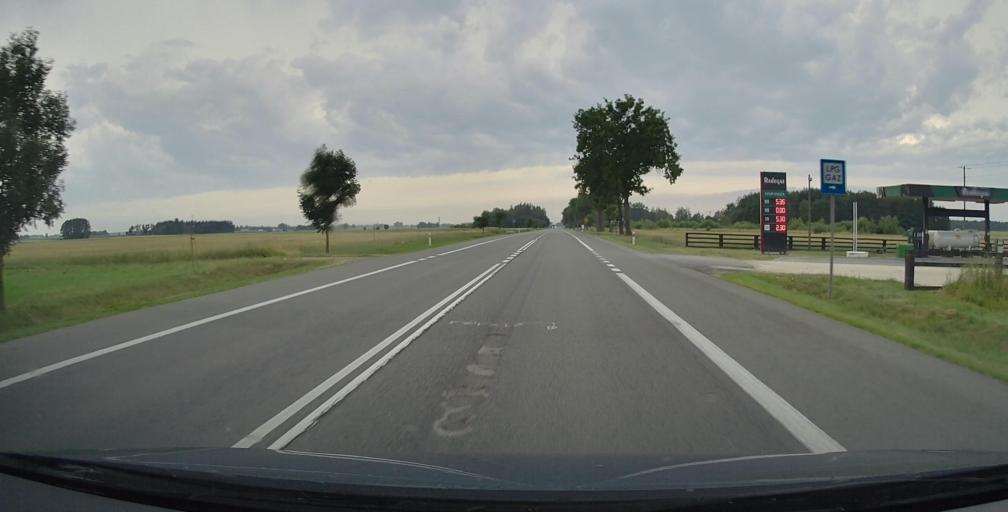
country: PL
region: Lublin Voivodeship
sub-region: Powiat lukowski
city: Trzebieszow
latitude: 52.0575
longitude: 22.6029
